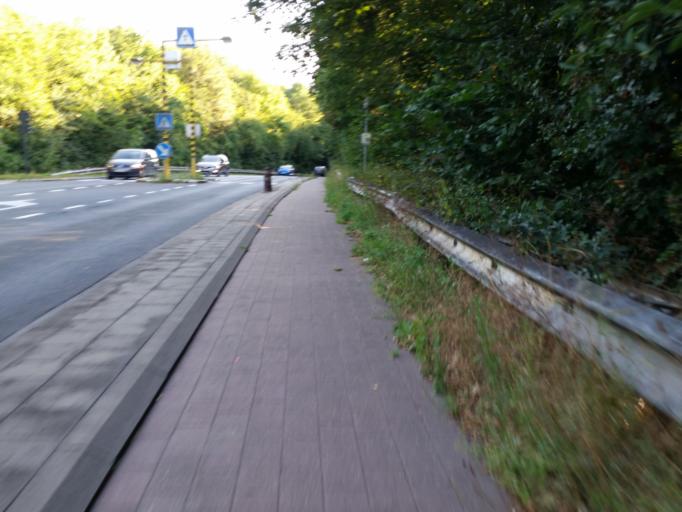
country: BE
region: Flanders
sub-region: Provincie Vlaams-Brabant
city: Machelen
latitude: 50.9251
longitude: 4.4637
